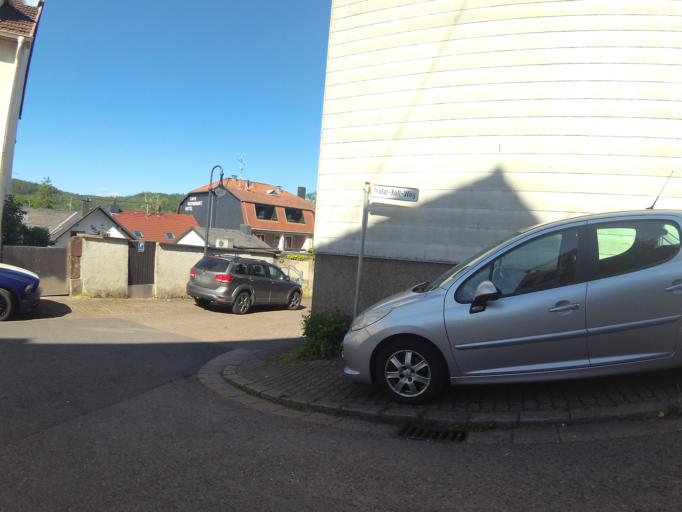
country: DE
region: Saarland
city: Mettlach
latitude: 49.4918
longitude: 6.5913
